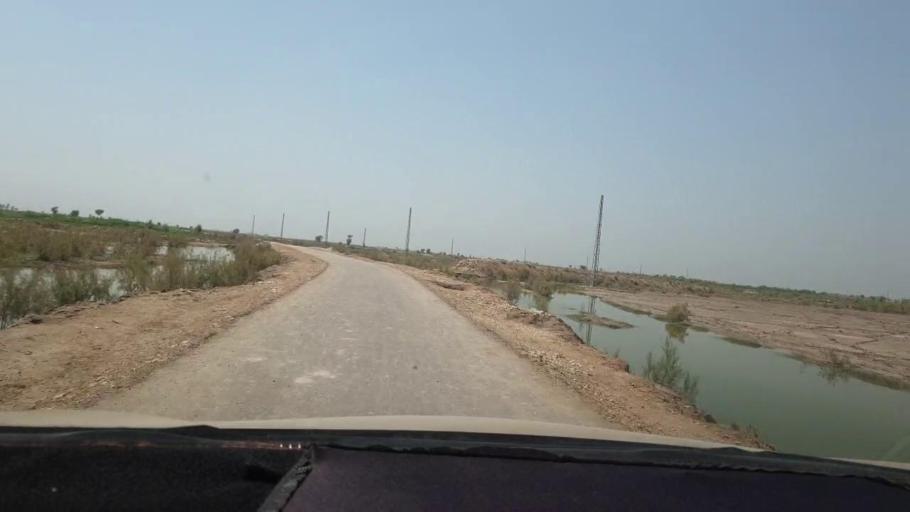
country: PK
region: Sindh
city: Shahdadkot
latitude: 27.8339
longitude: 67.8828
